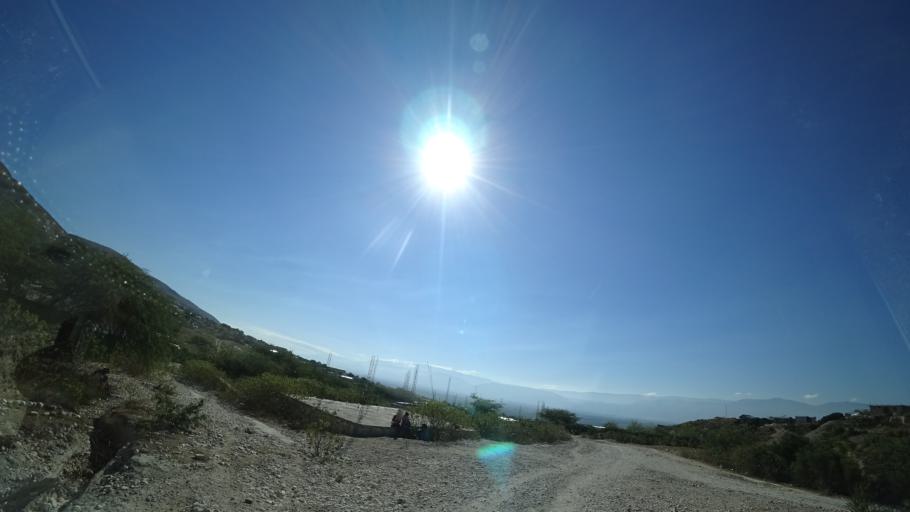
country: HT
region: Ouest
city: Croix des Bouquets
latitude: 18.6771
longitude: -72.2431
